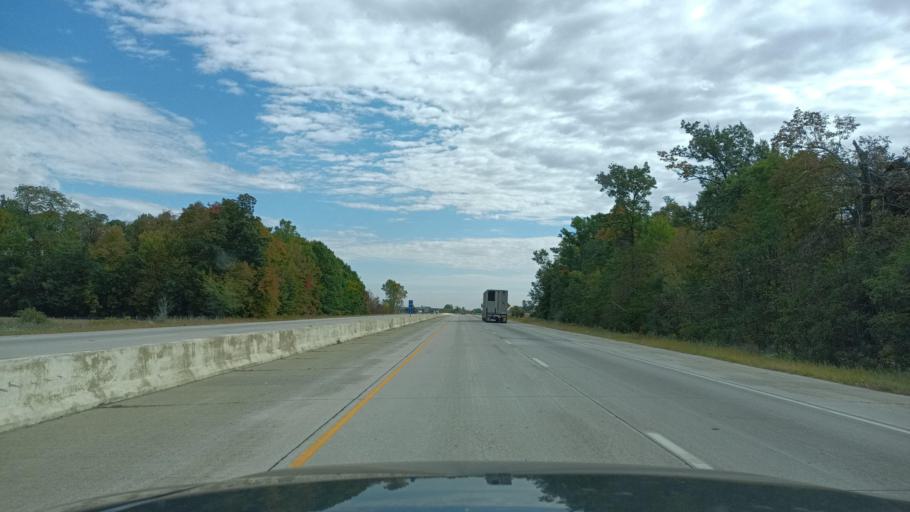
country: US
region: Indiana
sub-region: Wells County
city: Ossian
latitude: 40.9558
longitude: -85.1504
